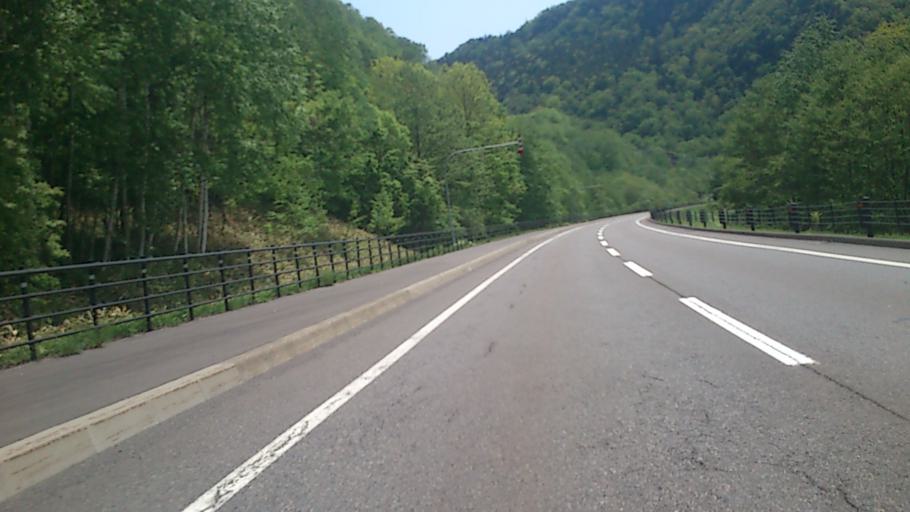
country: JP
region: Hokkaido
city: Otofuke
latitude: 43.3675
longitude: 143.2331
